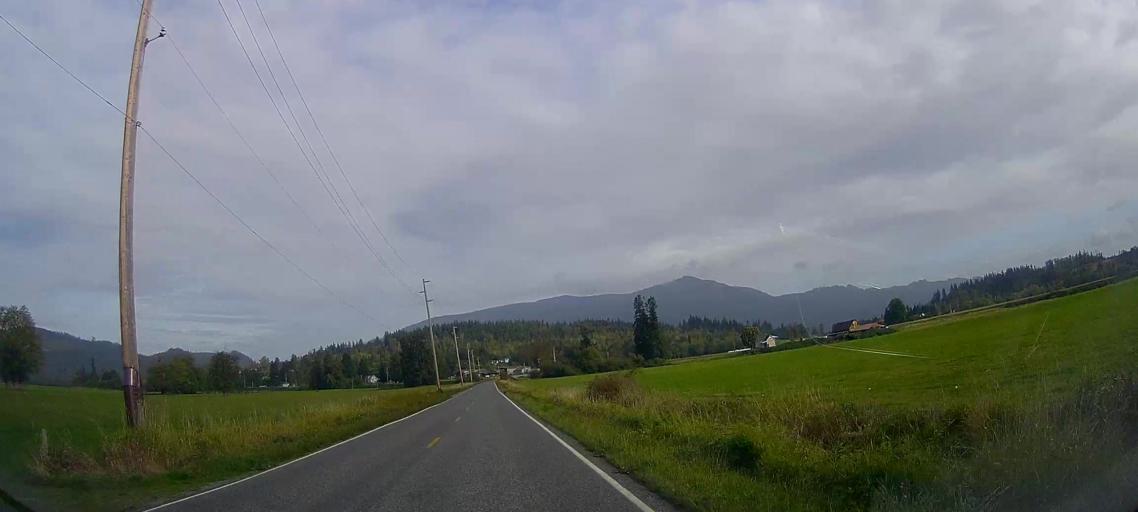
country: US
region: Washington
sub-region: Skagit County
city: Clear Lake
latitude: 48.4536
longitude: -122.2697
